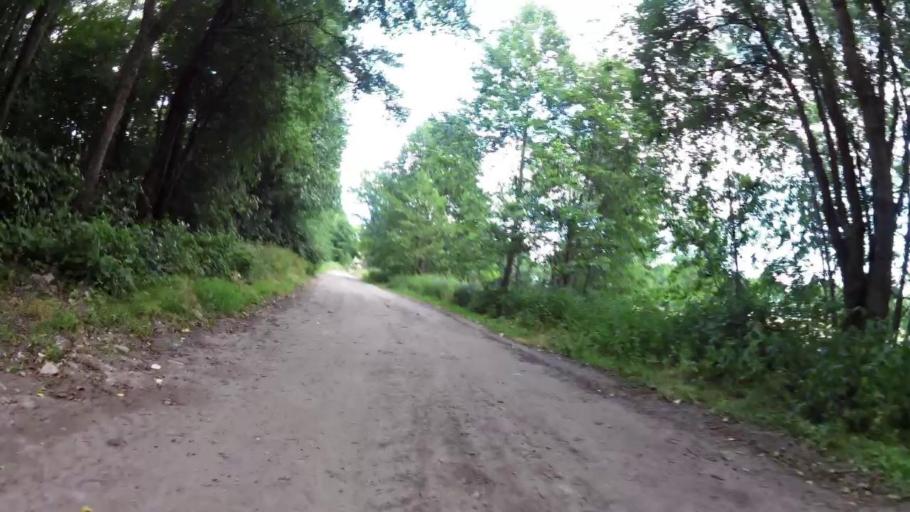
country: PL
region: West Pomeranian Voivodeship
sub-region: Powiat swidwinski
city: Swidwin
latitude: 53.6806
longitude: 15.7438
